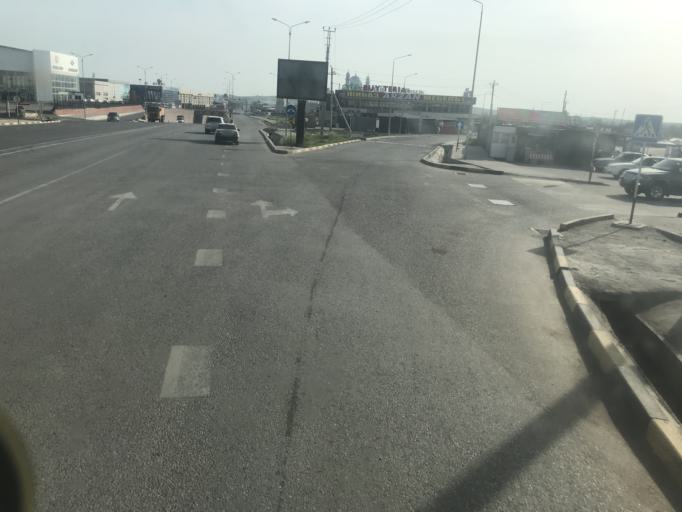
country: KZ
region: Ongtustik Qazaqstan
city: Shymkent
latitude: 42.3546
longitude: 69.5327
